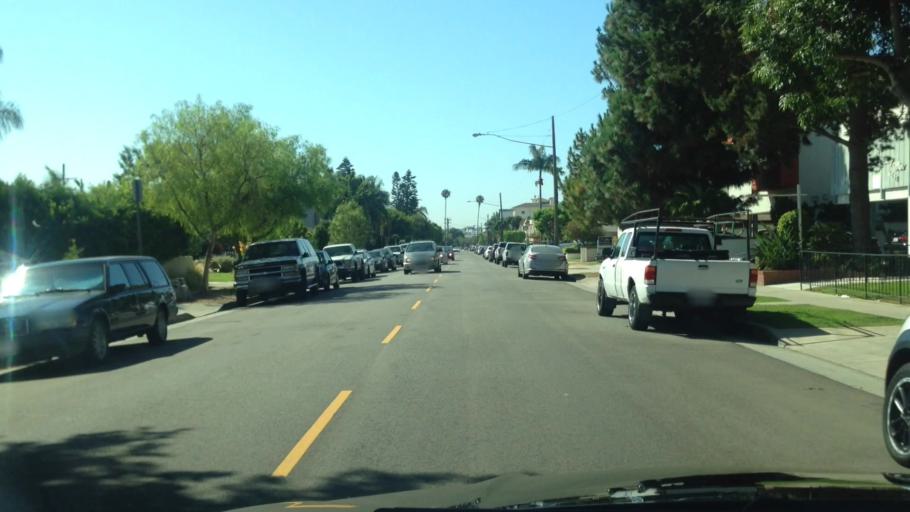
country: US
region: California
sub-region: Los Angeles County
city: Culver City
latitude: 34.0037
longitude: -118.4207
